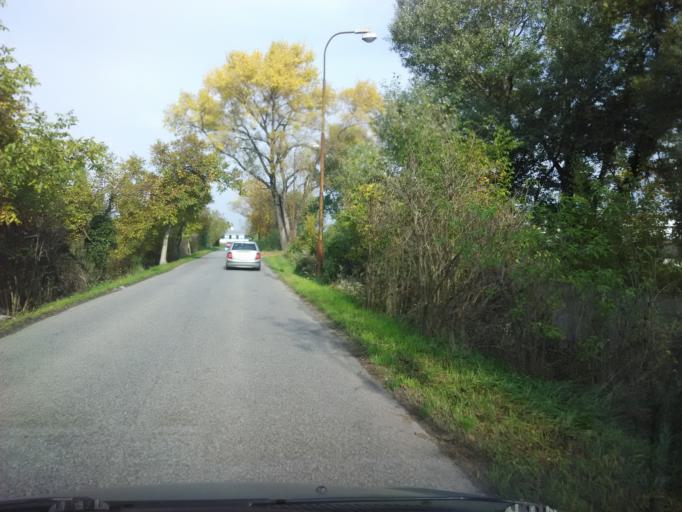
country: SK
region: Nitriansky
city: Komarno
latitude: 47.7606
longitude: 18.0960
